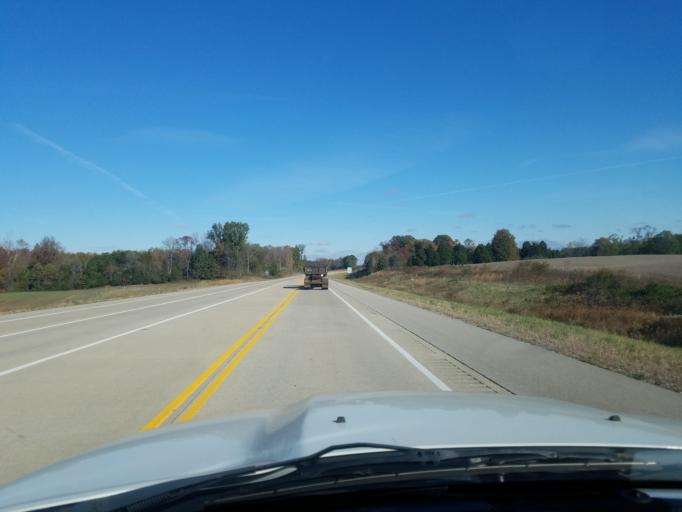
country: US
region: Indiana
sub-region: Jennings County
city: North Vernon
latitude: 39.0084
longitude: -85.6638
